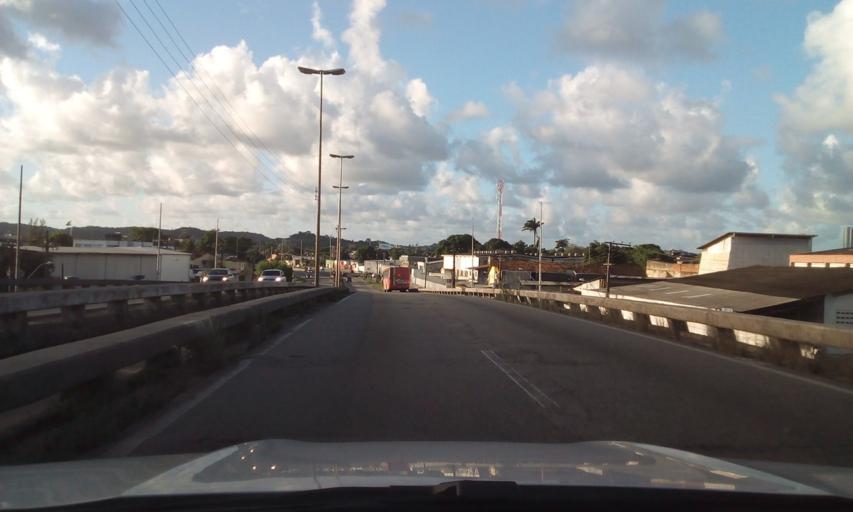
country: BR
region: Pernambuco
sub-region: Recife
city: Recife
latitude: -8.0388
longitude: -34.9419
